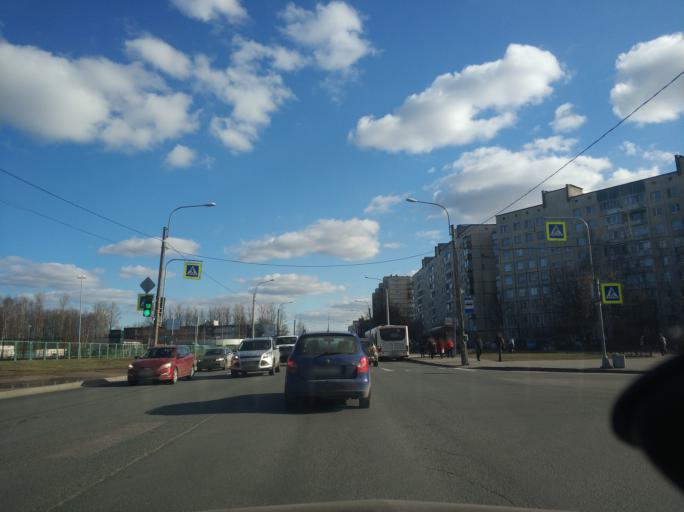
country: RU
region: St.-Petersburg
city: Krasnogvargeisky
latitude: 59.9571
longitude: 30.4936
